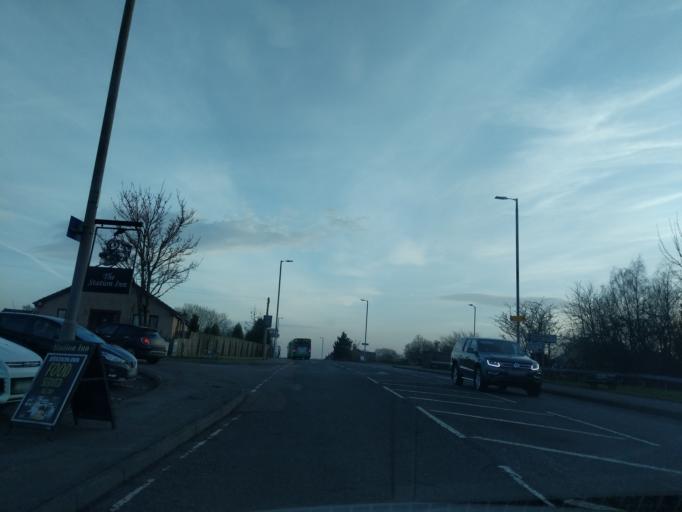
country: GB
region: Scotland
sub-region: South Lanarkshire
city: Carluke
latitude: 55.7153
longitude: -3.8323
